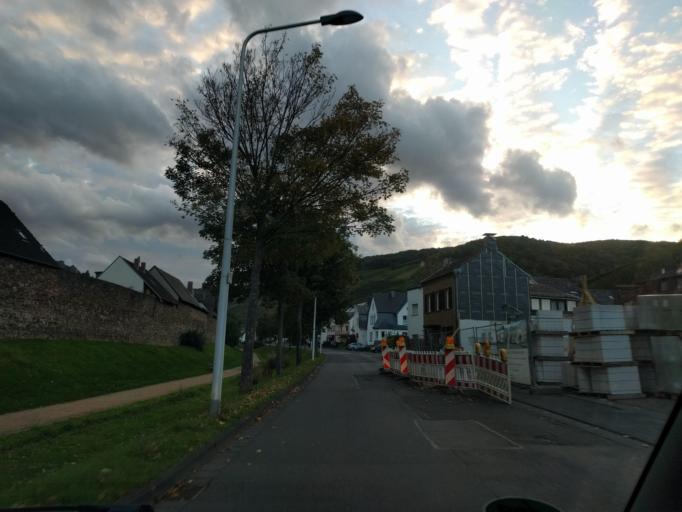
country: DE
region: Rheinland-Pfalz
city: Bad Neuenahr-Ahrweiler
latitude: 50.5444
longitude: 7.0971
